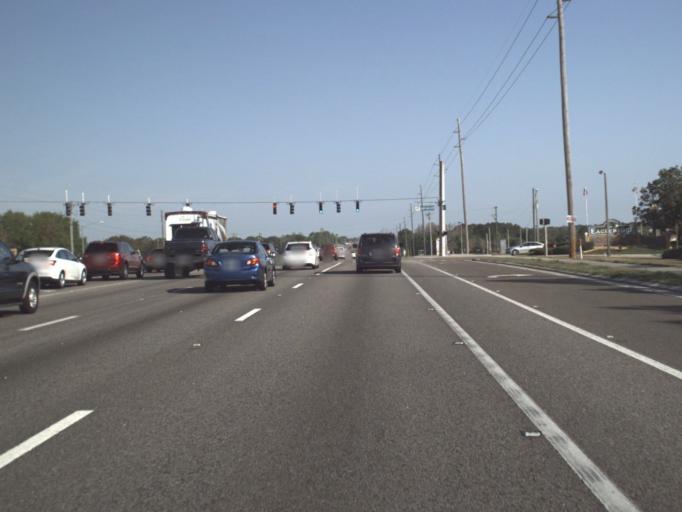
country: US
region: Florida
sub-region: Lake County
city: Four Corners
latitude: 28.3784
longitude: -81.6868
